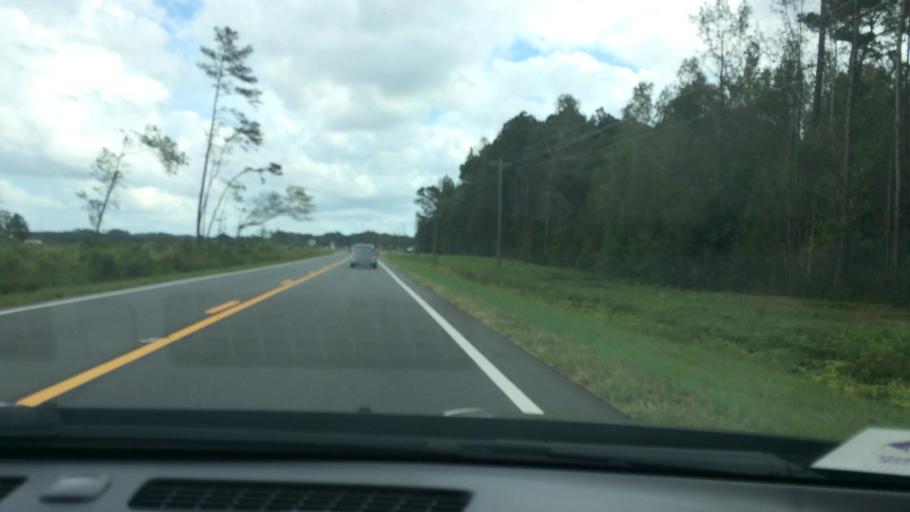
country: US
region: North Carolina
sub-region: Pitt County
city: Farmville
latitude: 35.5962
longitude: -77.6311
